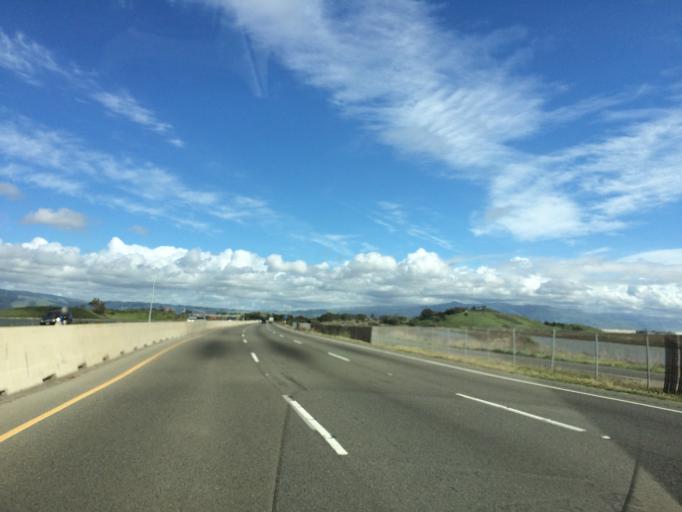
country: US
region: California
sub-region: Alameda County
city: Newark
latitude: 37.5326
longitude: -122.0873
